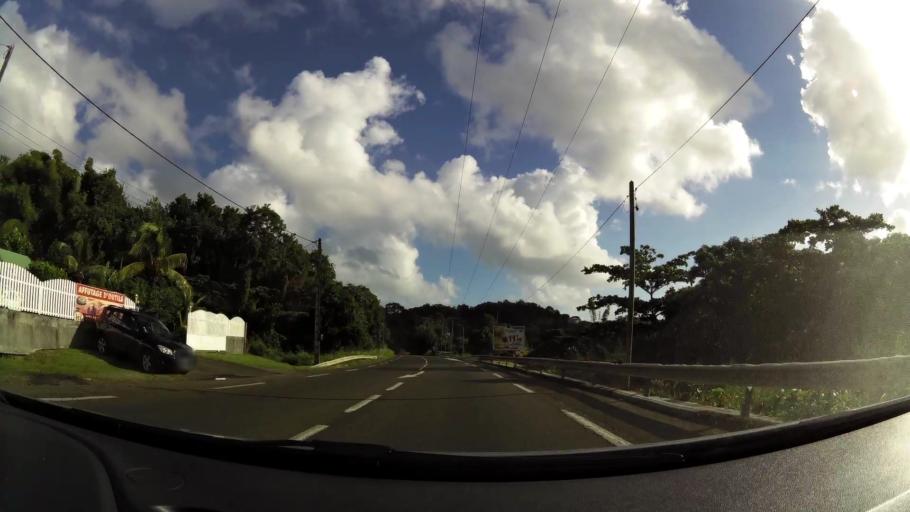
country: MQ
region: Martinique
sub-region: Martinique
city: Le Francois
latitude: 14.6008
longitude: -60.9409
